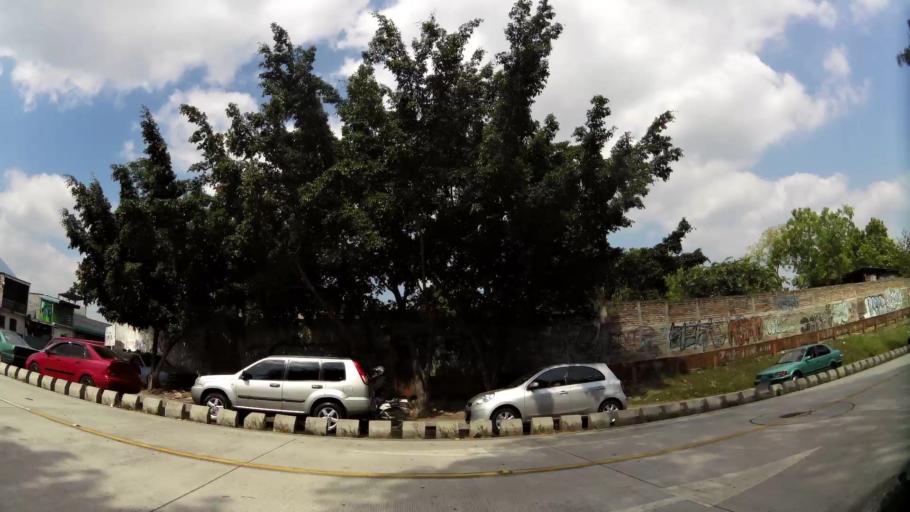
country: SV
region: San Salvador
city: San Salvador
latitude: 13.7025
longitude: -89.2057
